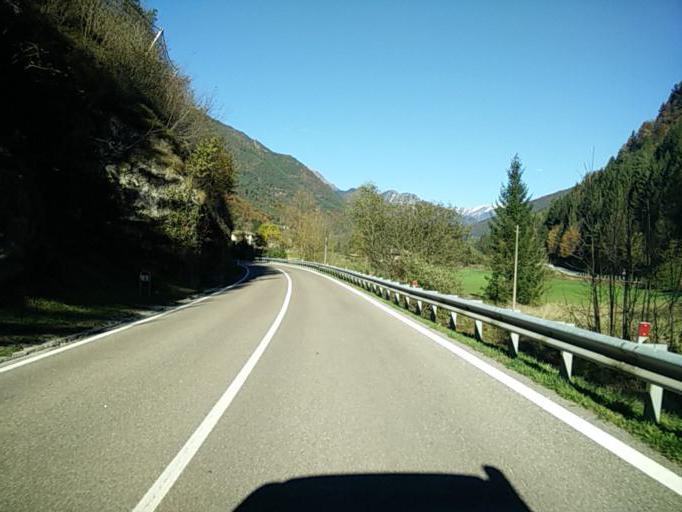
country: IT
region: Trentino-Alto Adige
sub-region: Provincia di Trento
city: Condino
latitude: 45.8646
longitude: 10.6457
